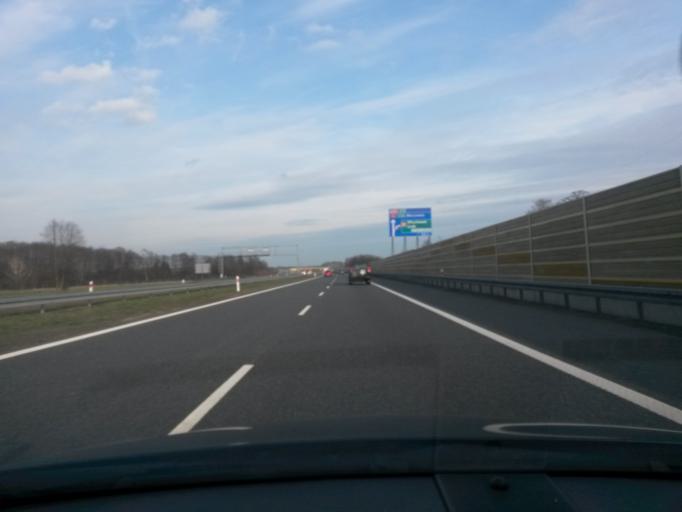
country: PL
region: Lodz Voivodeship
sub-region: Powiat zgierski
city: Ozorkow
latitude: 51.9236
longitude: 19.3394
